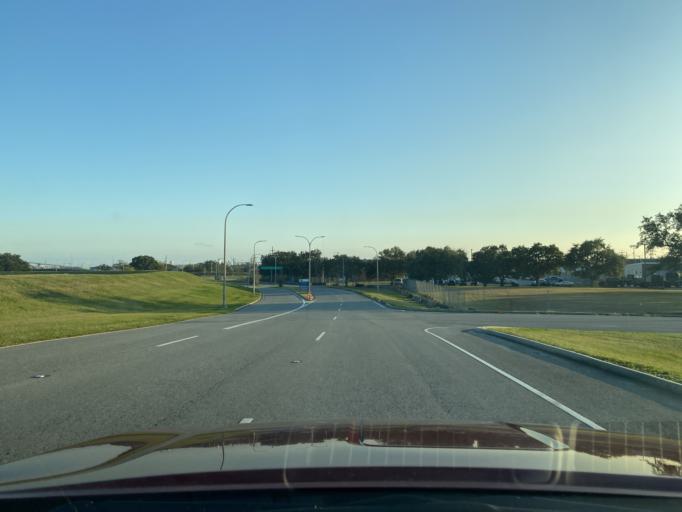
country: US
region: Louisiana
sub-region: Orleans Parish
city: New Orleans
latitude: 30.0331
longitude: -90.0414
